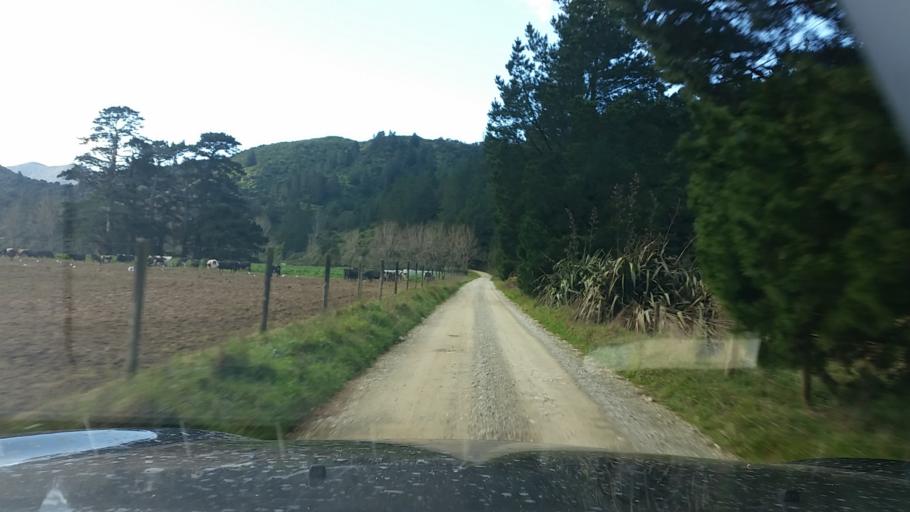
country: NZ
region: Marlborough
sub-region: Marlborough District
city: Picton
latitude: -41.1424
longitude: 174.1381
